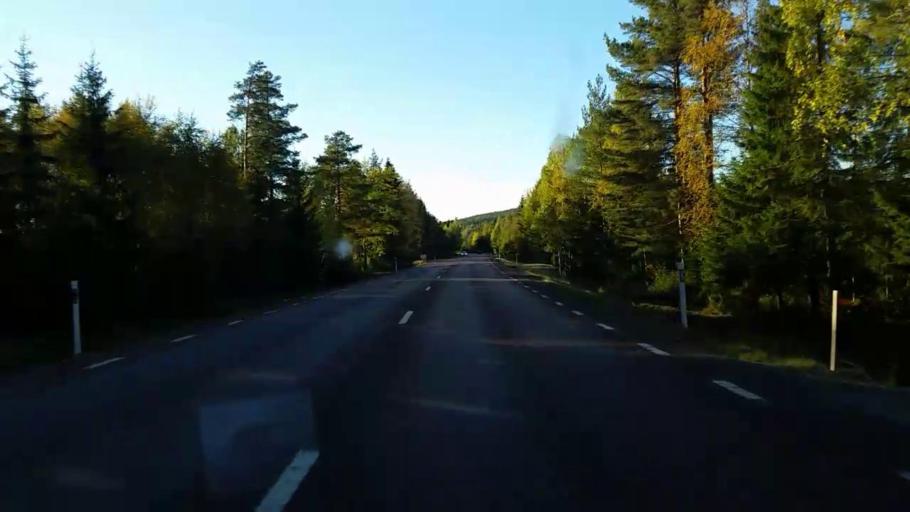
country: SE
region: Gaevleborg
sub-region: Ljusdals Kommun
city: Jaervsoe
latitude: 61.8124
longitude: 16.2079
